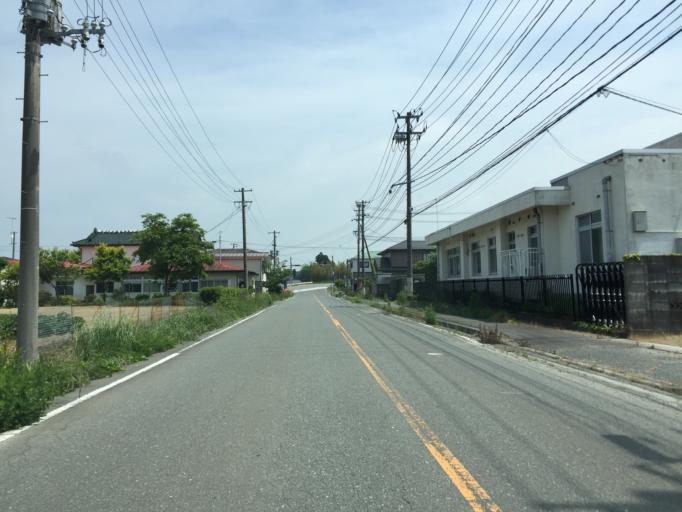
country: JP
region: Fukushima
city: Namie
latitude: 37.4877
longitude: 140.9959
